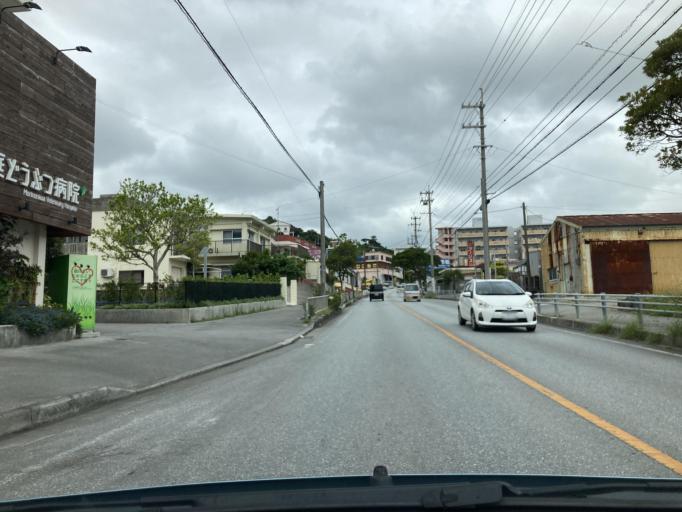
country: JP
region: Okinawa
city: Ginowan
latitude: 26.2318
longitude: 127.7529
